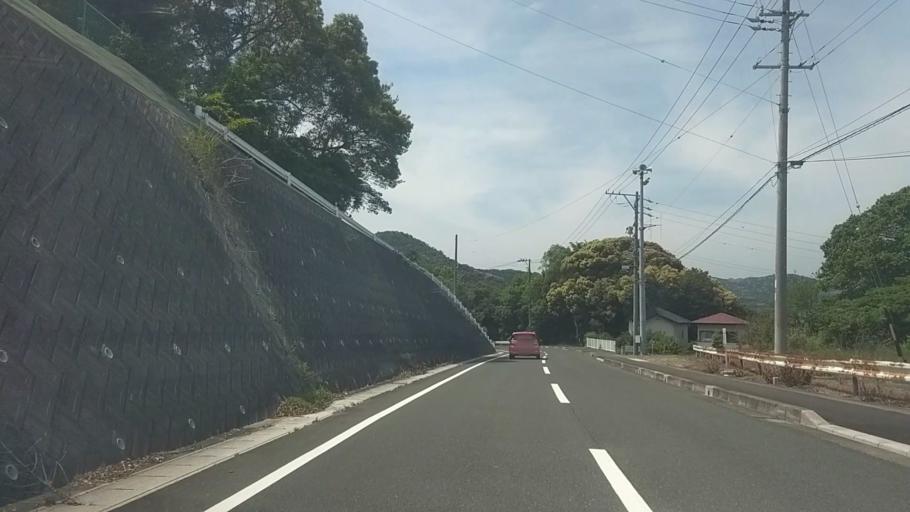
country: JP
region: Shizuoka
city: Kosai-shi
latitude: 34.7694
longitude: 137.5528
